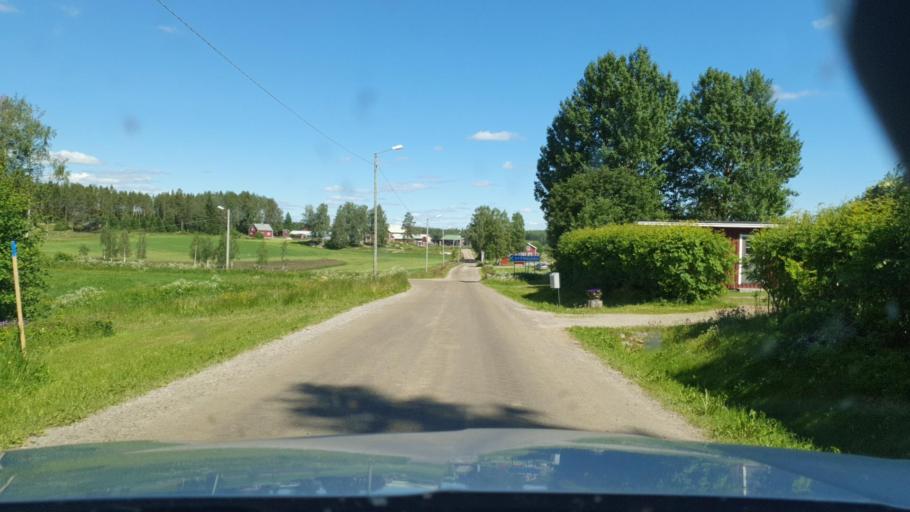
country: SE
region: Vaesterbotten
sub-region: Skelleftea Kommun
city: Byske
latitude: 65.1195
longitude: 21.2107
